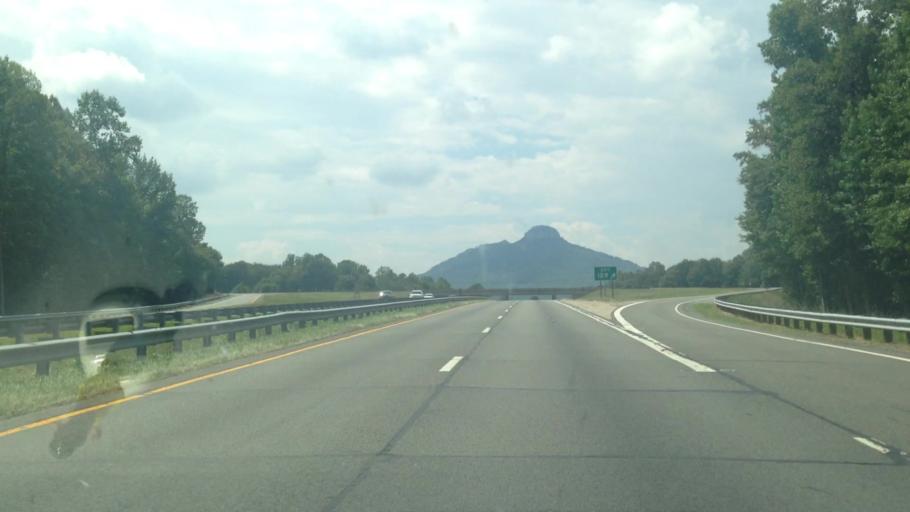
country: US
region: North Carolina
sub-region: Surry County
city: Pilot Mountain
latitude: 36.3152
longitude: -80.4352
